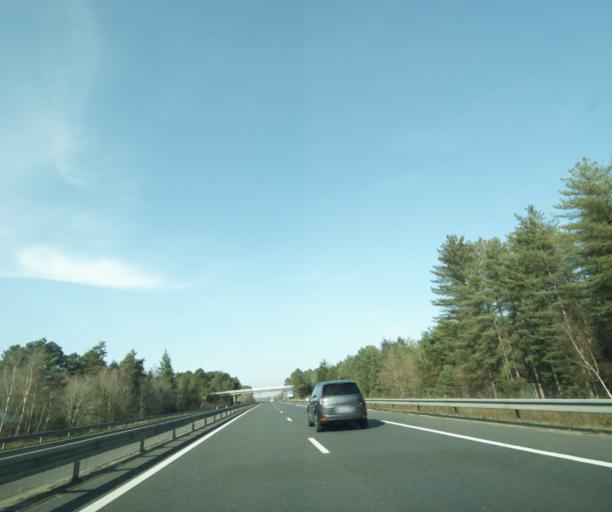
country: FR
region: Centre
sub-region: Departement du Loir-et-Cher
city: Nouan-le-Fuzelier
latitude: 47.5335
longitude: 2.0045
